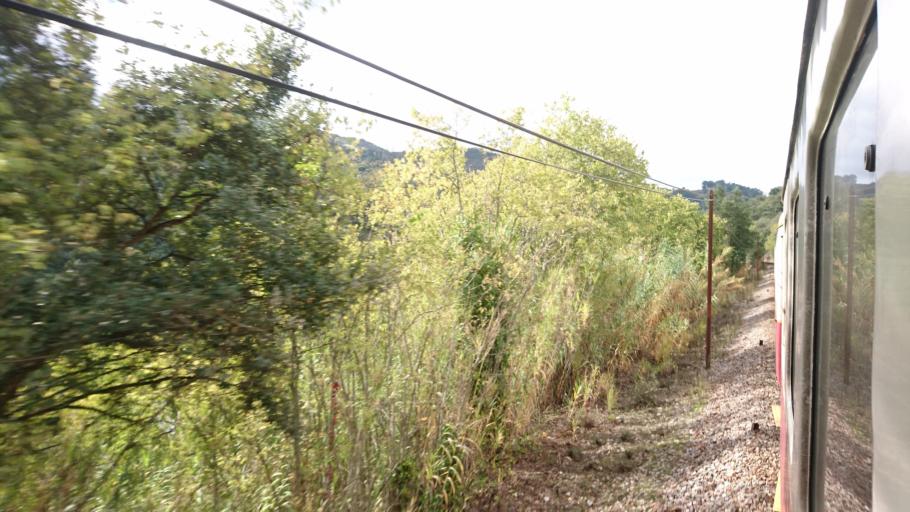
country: PT
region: Viseu
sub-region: Resende
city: Resende
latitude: 41.1212
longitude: -7.9201
